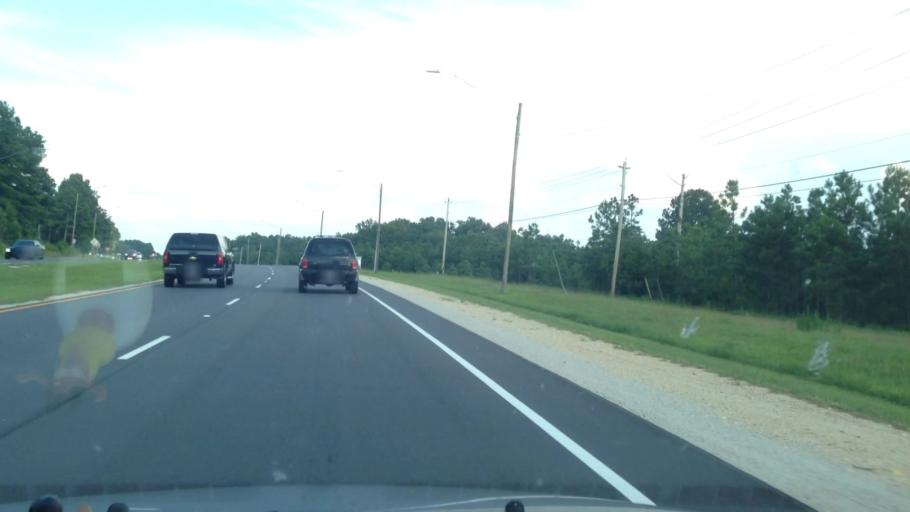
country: US
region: North Carolina
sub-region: Harnett County
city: Lillington
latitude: 35.4115
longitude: -78.7906
